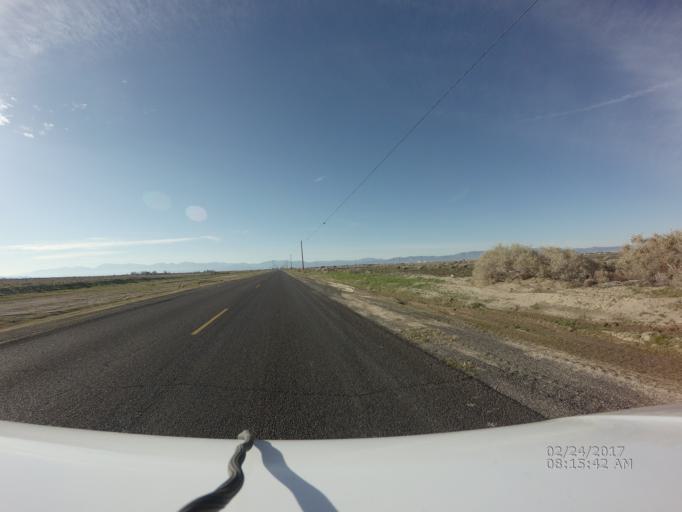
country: US
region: California
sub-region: Los Angeles County
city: Lancaster
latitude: 34.7331
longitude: -118.0411
